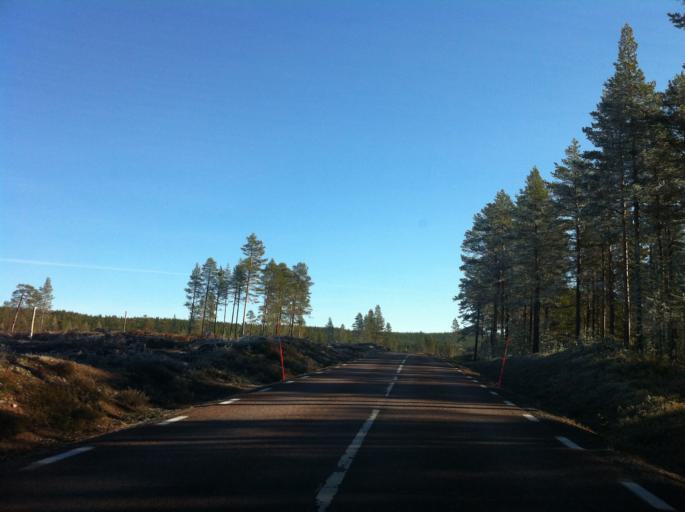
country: NO
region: Hedmark
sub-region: Trysil
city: Innbygda
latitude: 61.8447
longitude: 12.7833
